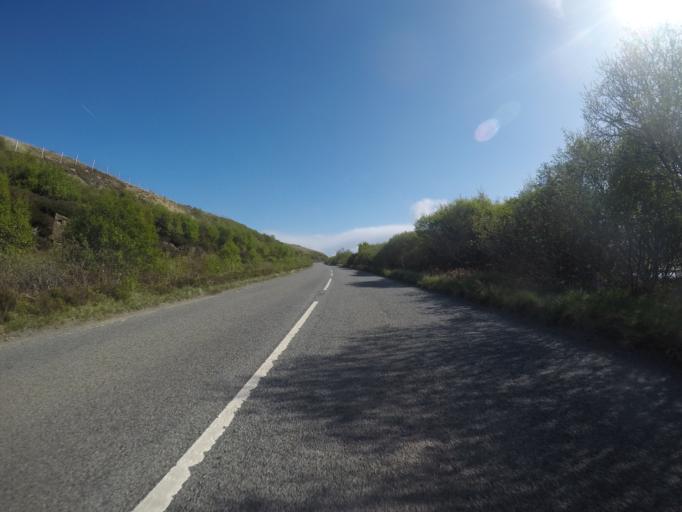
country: GB
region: Scotland
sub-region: Highland
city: Portree
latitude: 57.6080
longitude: -6.1738
